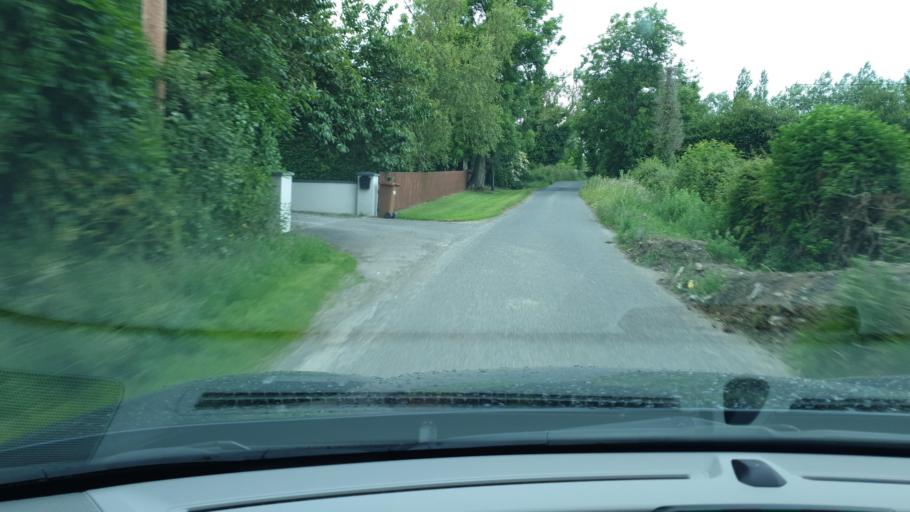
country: IE
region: Leinster
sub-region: An Mhi
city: Ashbourne
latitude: 53.5291
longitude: -6.3906
